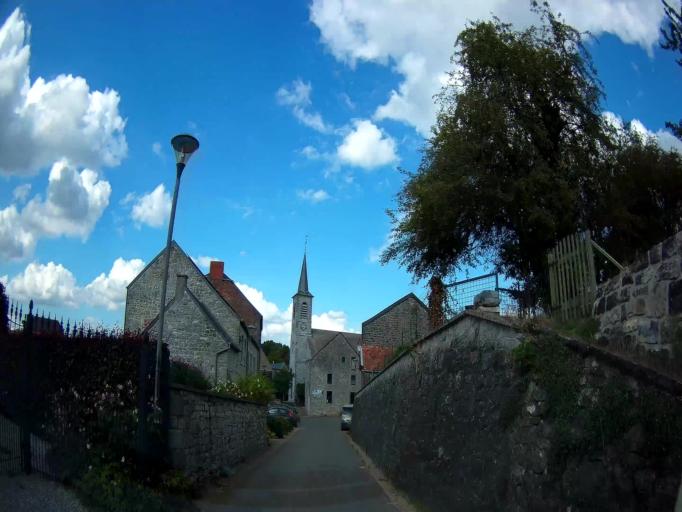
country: BE
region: Wallonia
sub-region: Province de Namur
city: Onhaye
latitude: 50.2778
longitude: 4.7937
